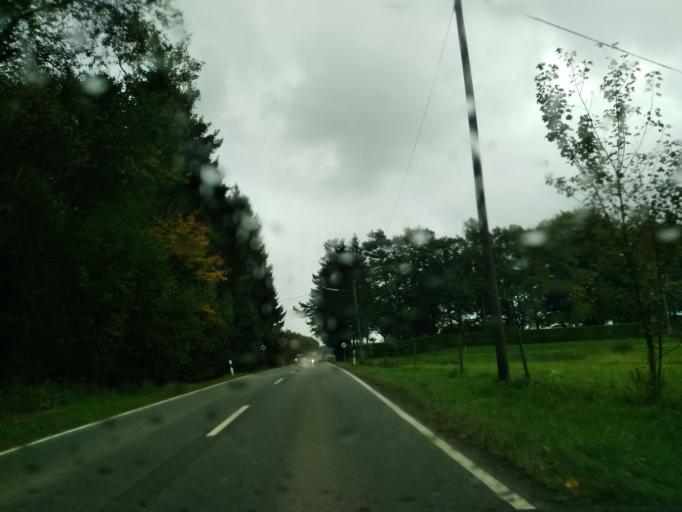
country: DE
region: Rheinland-Pfalz
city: Windhagen
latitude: 50.6612
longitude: 7.3572
